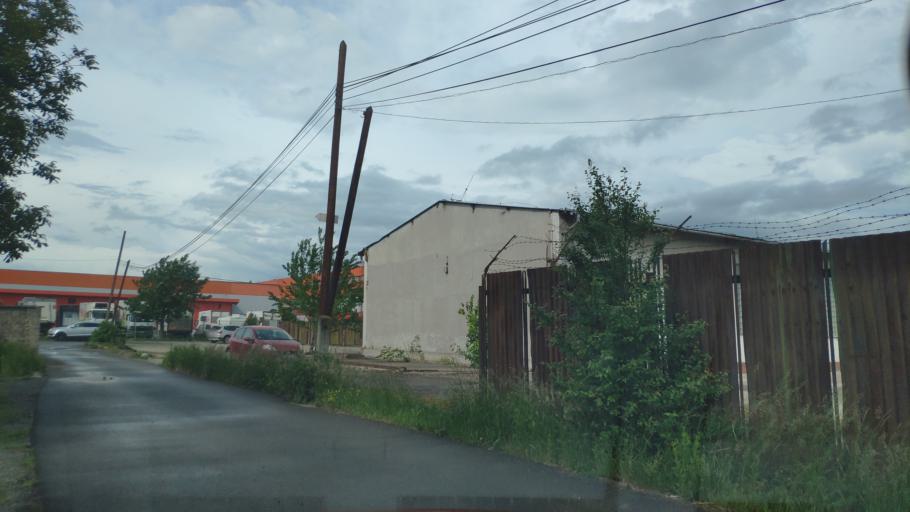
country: SK
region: Kosicky
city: Kosice
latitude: 48.6866
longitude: 21.2754
